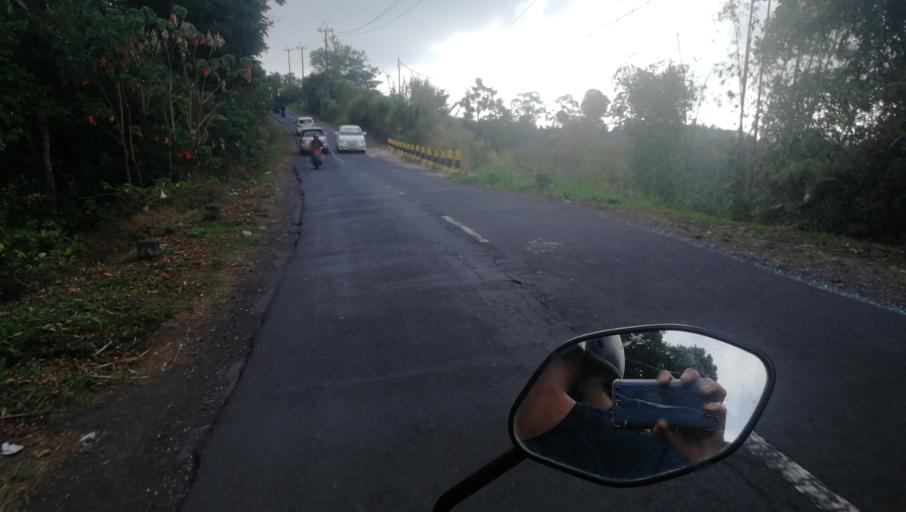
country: ID
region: Bali
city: Munduk
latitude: -8.2485
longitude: 115.0963
